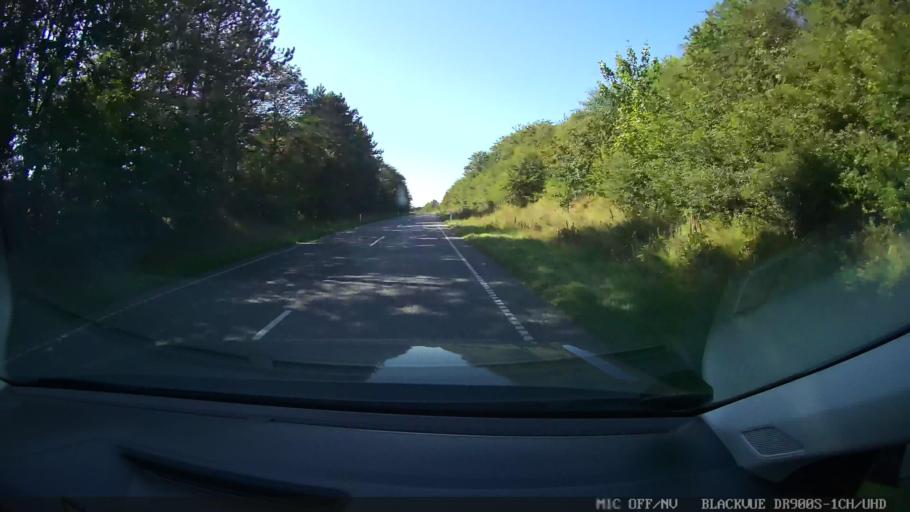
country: DK
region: North Denmark
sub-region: Mariagerfjord Kommune
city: Mariager
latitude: 56.6357
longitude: 9.9341
